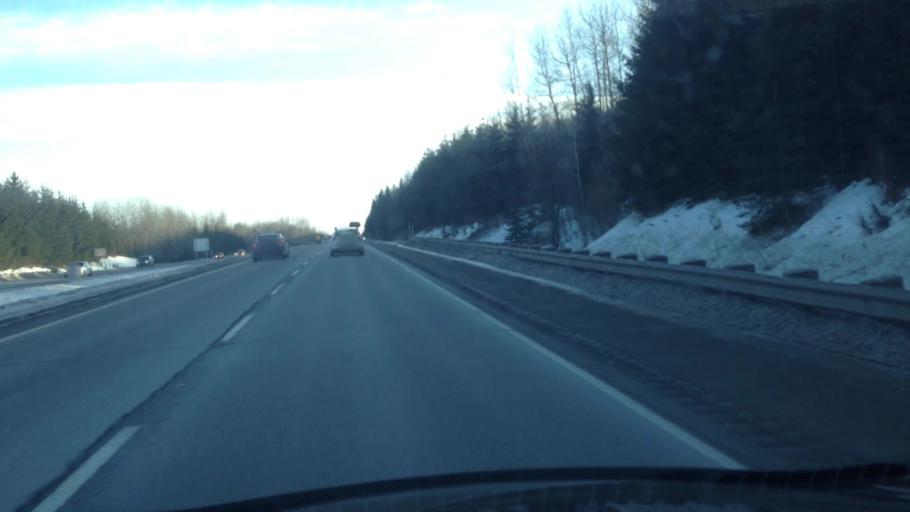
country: CA
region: Quebec
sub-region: Laurentides
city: Prevost
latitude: 45.8552
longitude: -74.0780
